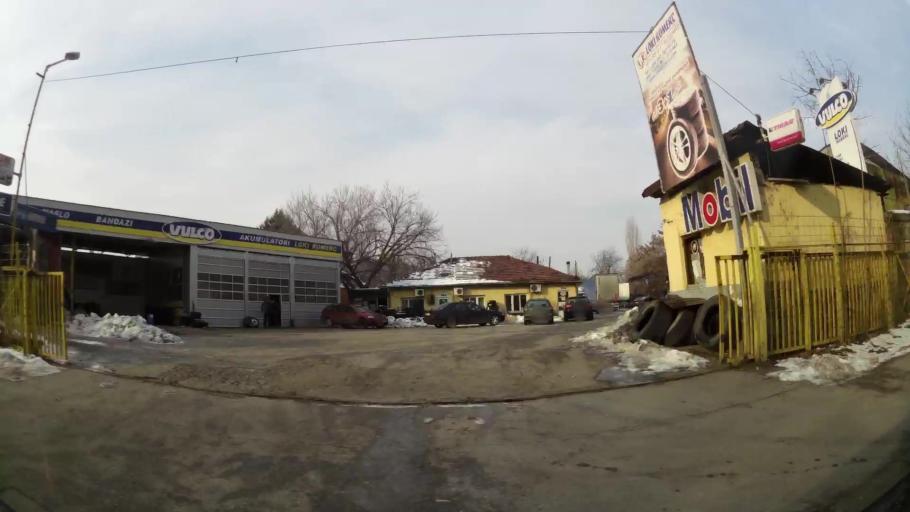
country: MK
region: Cair
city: Cair
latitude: 42.0169
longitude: 21.4310
